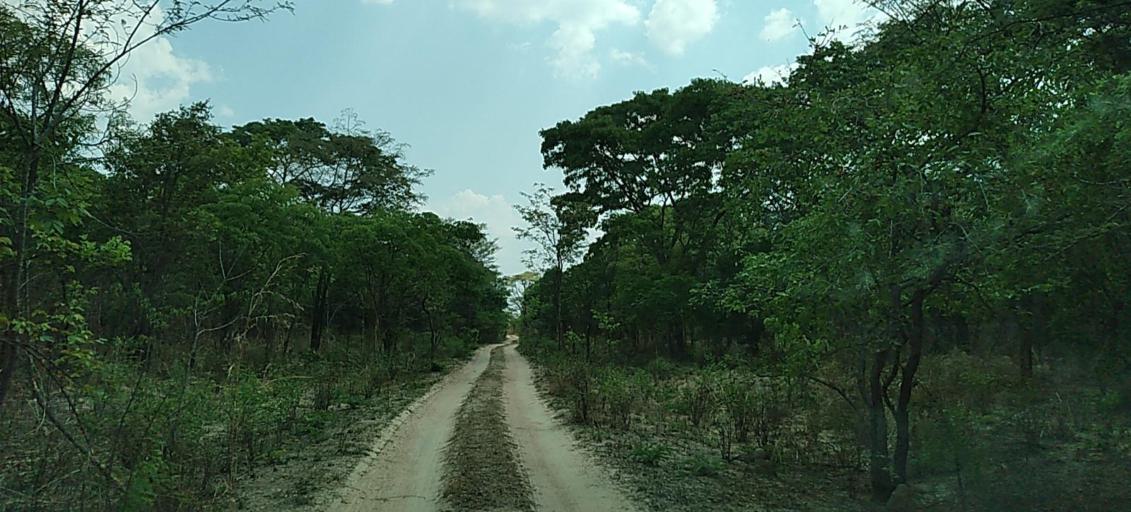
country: ZM
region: Copperbelt
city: Mpongwe
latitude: -13.8666
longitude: 27.9252
